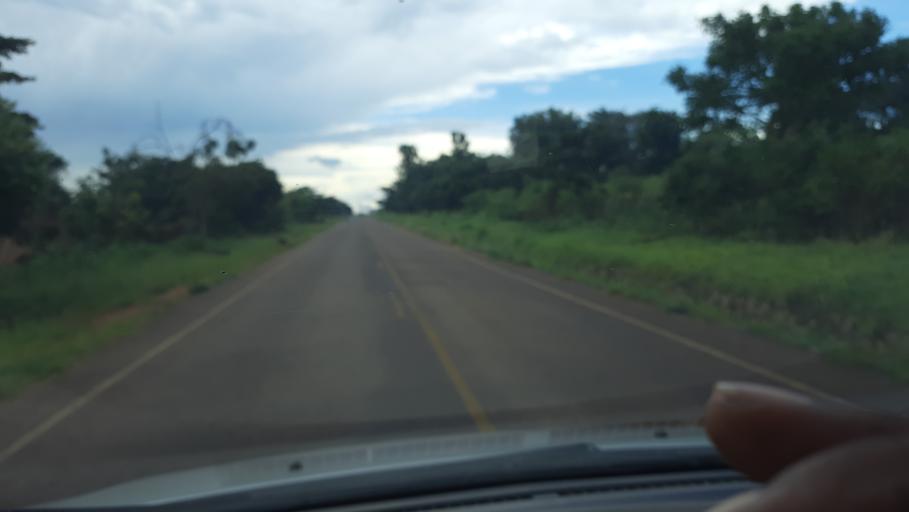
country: UG
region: Central Region
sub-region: Nakasongola District
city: Nakasongola
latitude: 1.3167
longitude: 32.4375
